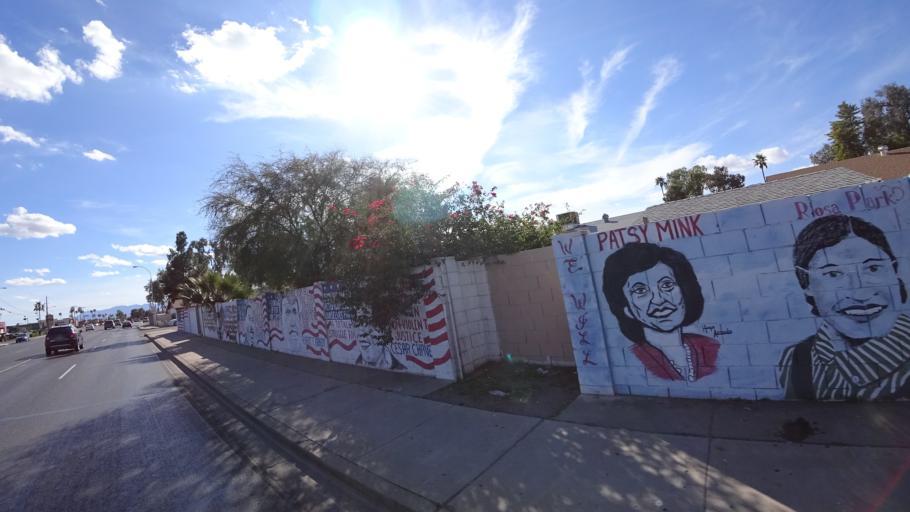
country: US
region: Arizona
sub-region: Maricopa County
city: Tolleson
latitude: 33.4830
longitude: -112.2207
